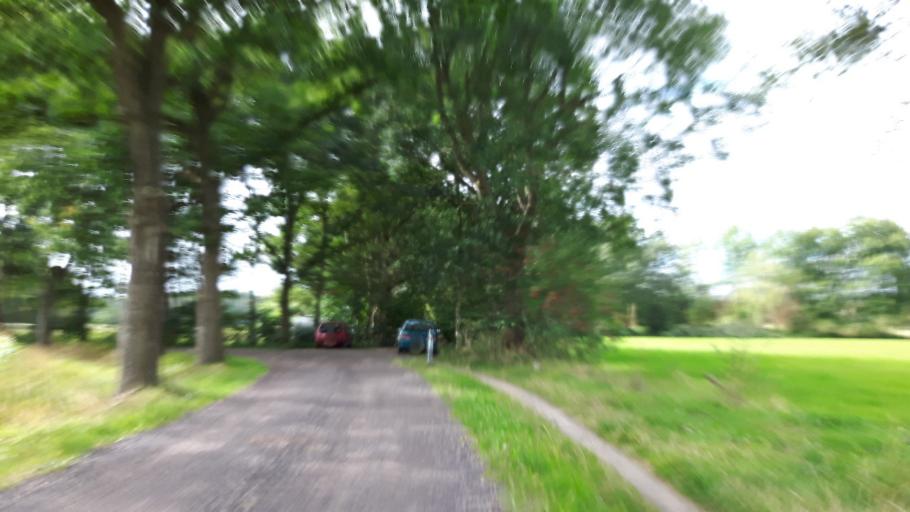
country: NL
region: Friesland
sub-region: Gemeente Heerenveen
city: Jubbega
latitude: 53.0412
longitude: 6.2627
